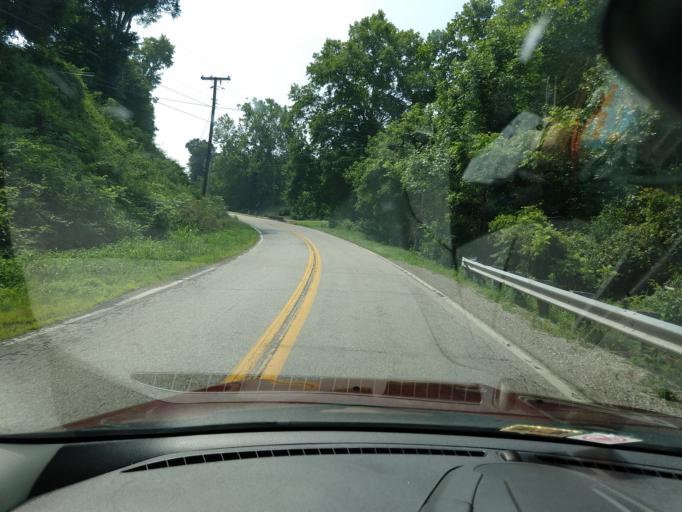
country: US
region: West Virginia
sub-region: Mason County
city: New Haven
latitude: 38.9367
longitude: -81.9189
